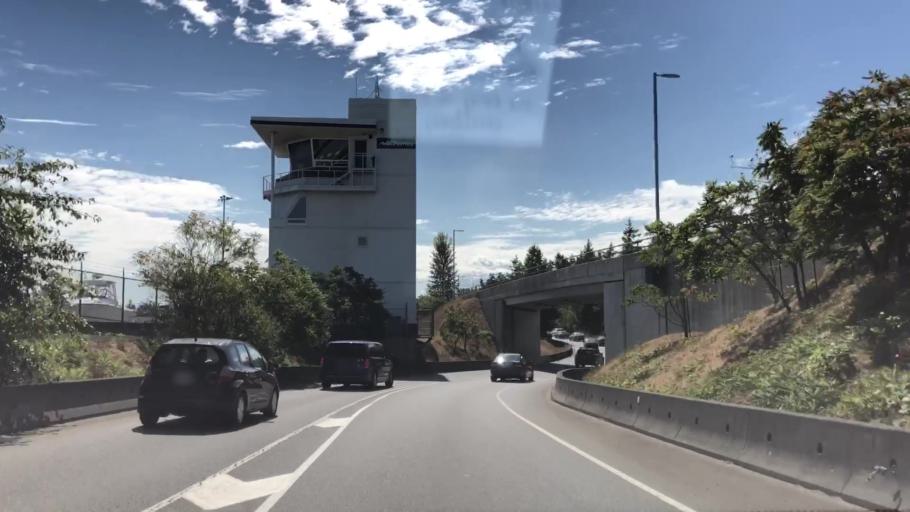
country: CA
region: British Columbia
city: Nanaimo
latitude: 49.1590
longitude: -123.8918
